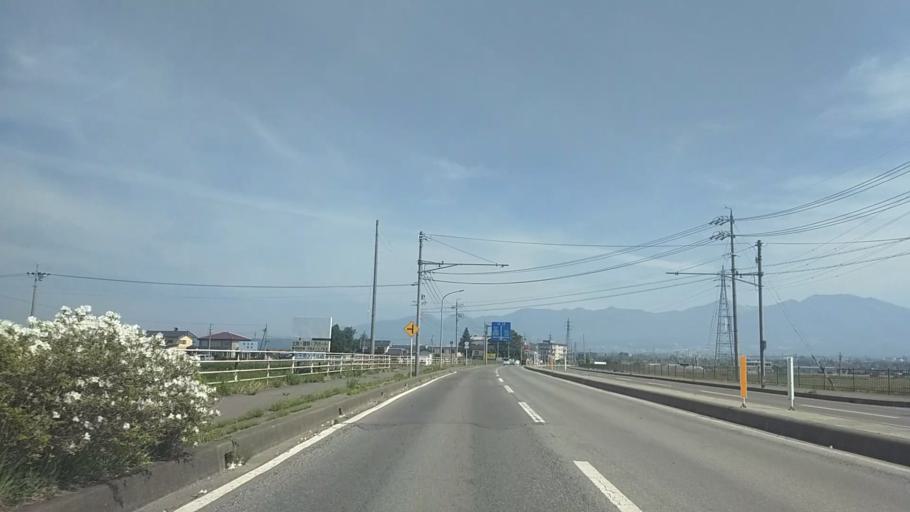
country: JP
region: Nagano
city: Saku
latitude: 36.2260
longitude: 138.4566
